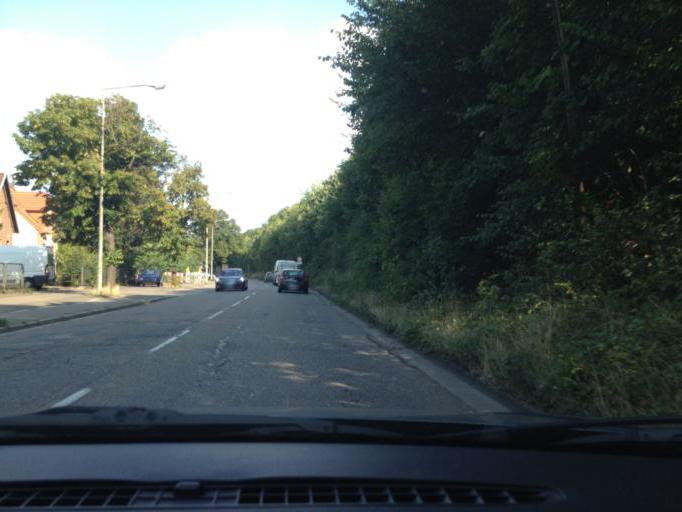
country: DE
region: Rheinland-Pfalz
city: Neustadt
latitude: 49.3513
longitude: 8.1223
